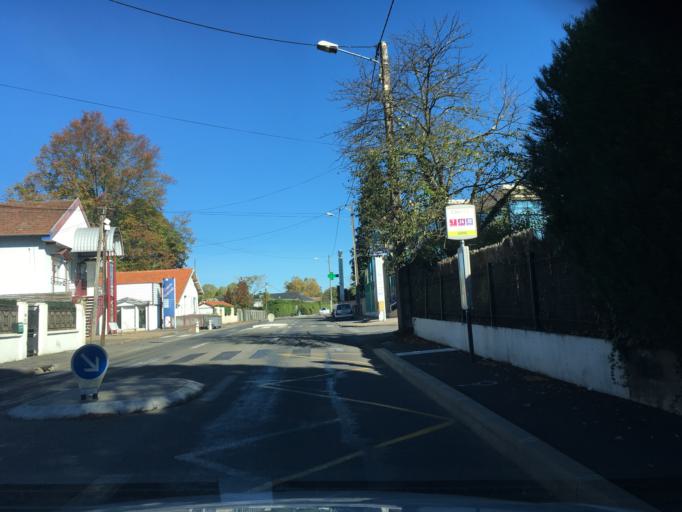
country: FR
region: Aquitaine
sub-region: Departement des Pyrenees-Atlantiques
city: Idron
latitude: 43.3010
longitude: -0.3316
